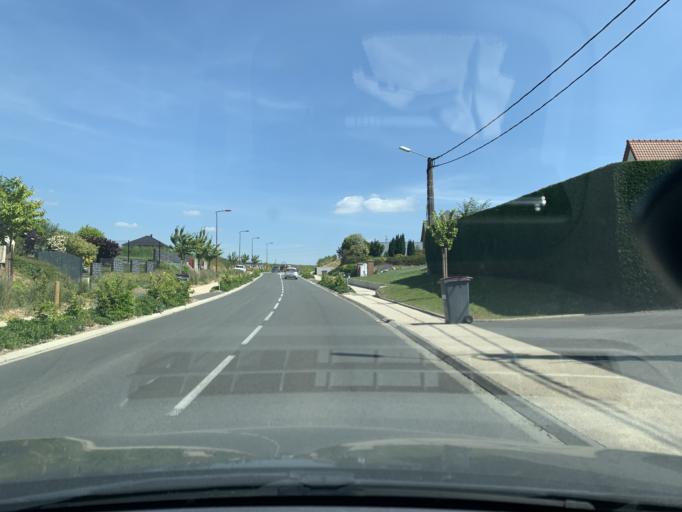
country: FR
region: Nord-Pas-de-Calais
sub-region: Departement du Nord
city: Fontaine-au-Pire
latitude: 50.1293
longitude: 3.3883
